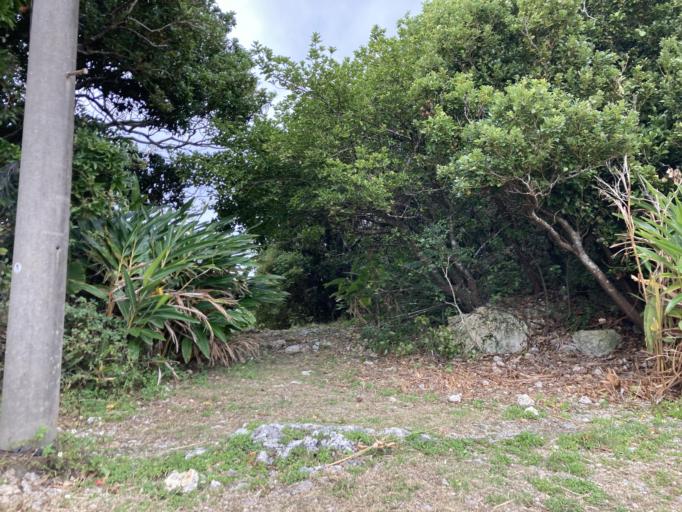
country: JP
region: Okinawa
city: Ginowan
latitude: 26.1625
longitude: 127.7891
